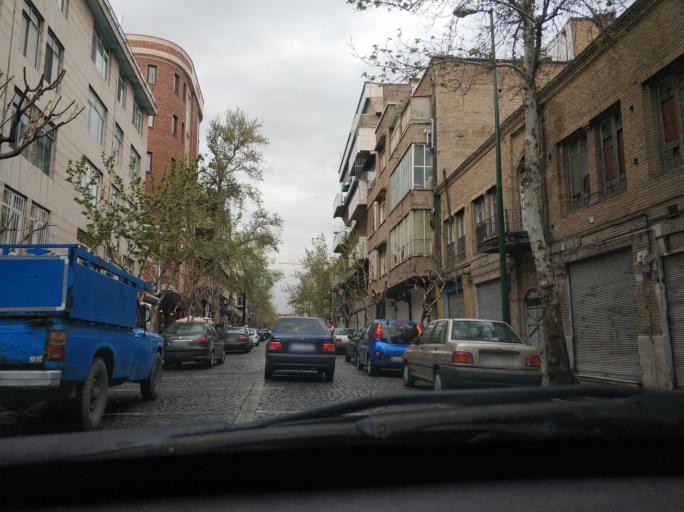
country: IR
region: Tehran
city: Tehran
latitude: 35.6924
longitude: 51.4143
